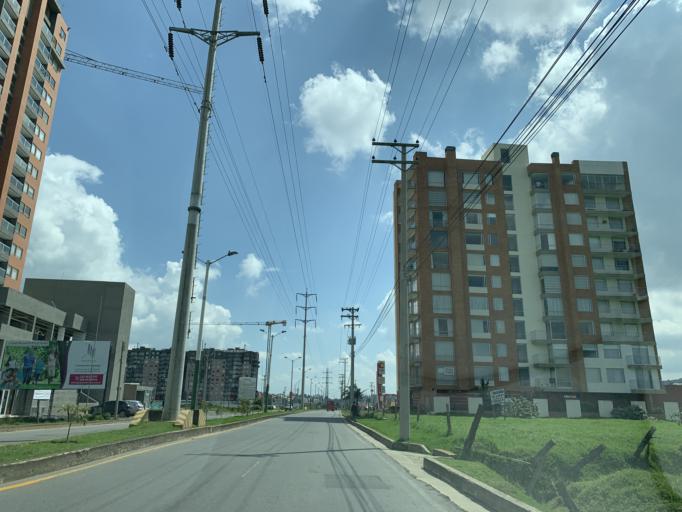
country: CO
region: Boyaca
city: Tunja
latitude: 5.5590
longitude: -73.3436
